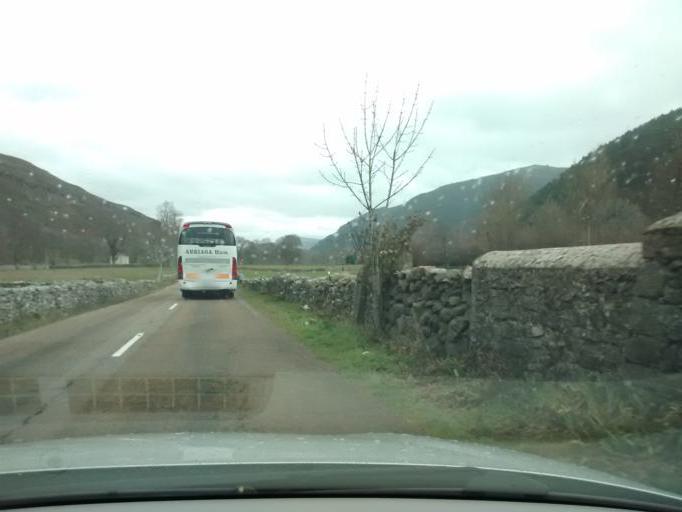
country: ES
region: Castille and Leon
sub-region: Provincia de Burgos
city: Espinosa de los Monteros
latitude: 43.1106
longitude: -3.5780
